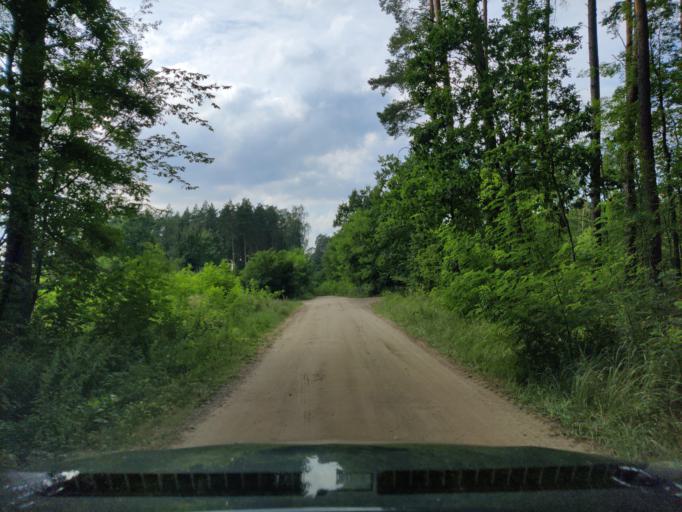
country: PL
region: Masovian Voivodeship
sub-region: Powiat pultuski
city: Pultusk
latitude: 52.6900
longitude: 21.1670
